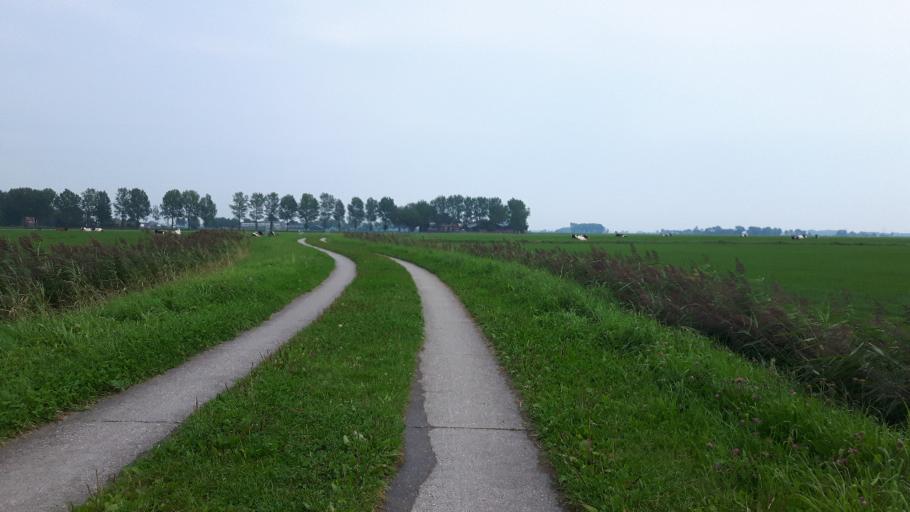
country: NL
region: Groningen
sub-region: Gemeente Winsum
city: Winsum
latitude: 53.3318
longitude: 6.5382
